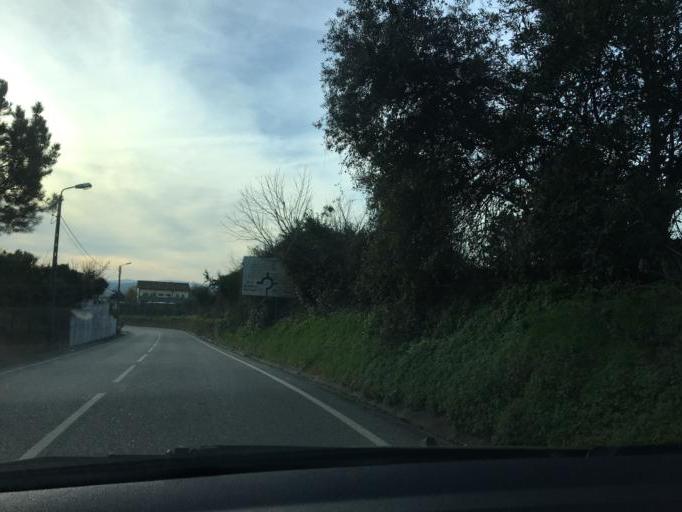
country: PT
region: Coimbra
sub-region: Montemor-O-Velho
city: Montemor-o-Velho
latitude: 40.2006
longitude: -8.6472
